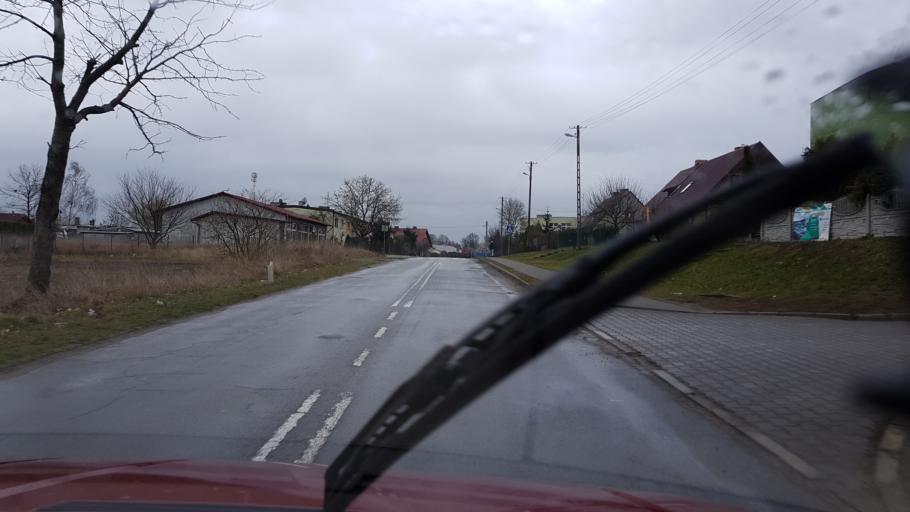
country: PL
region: West Pomeranian Voivodeship
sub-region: Powiat pyrzycki
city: Bielice
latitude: 53.2639
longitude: 14.6176
